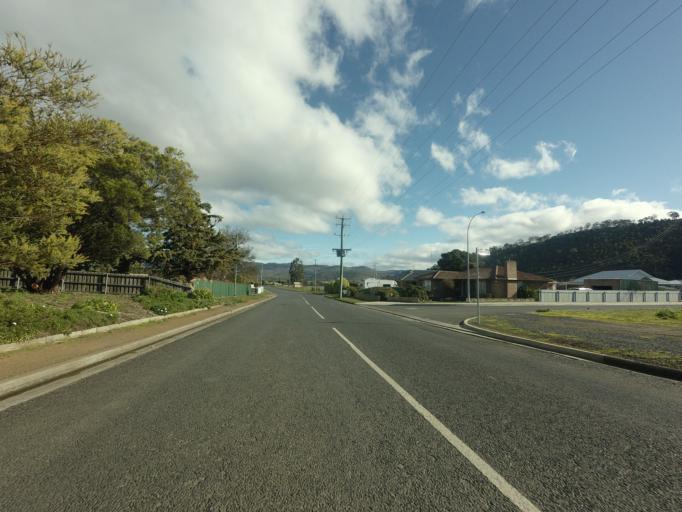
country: AU
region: Tasmania
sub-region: Derwent Valley
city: New Norfolk
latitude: -42.7573
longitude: 147.0494
